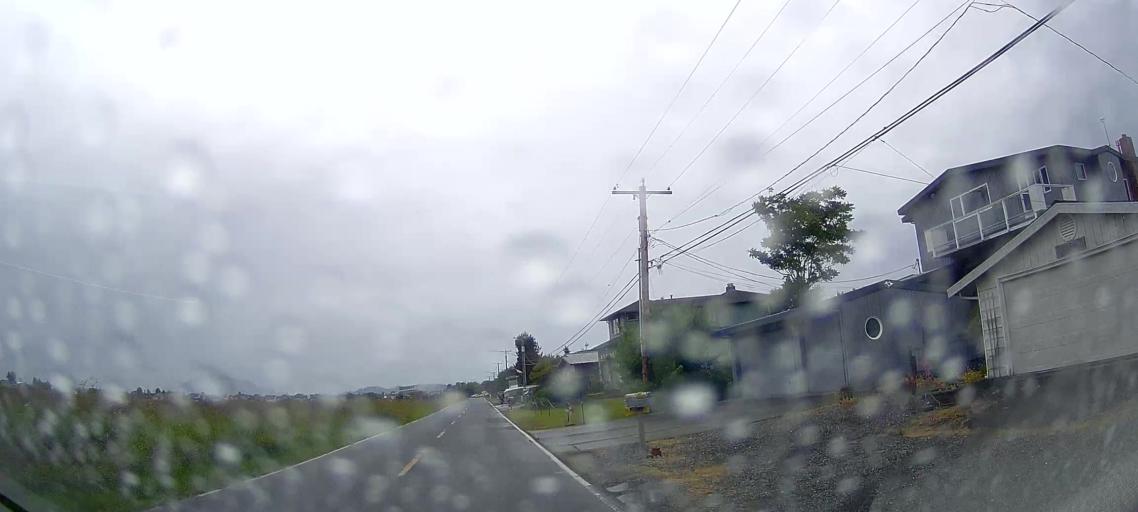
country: US
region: Washington
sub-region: Whatcom County
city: Birch Bay
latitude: 48.7967
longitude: -122.7103
